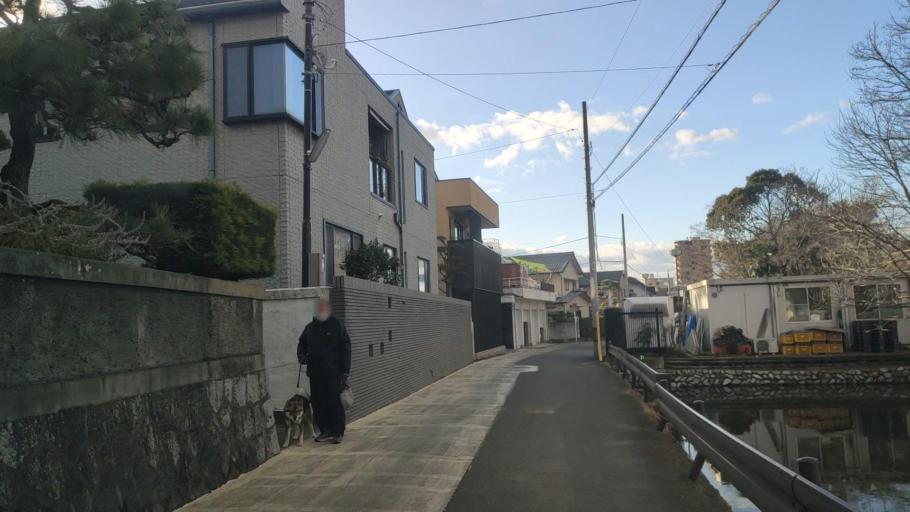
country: JP
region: Ehime
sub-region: Shikoku-chuo Shi
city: Matsuyama
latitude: 33.8489
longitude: 132.7884
